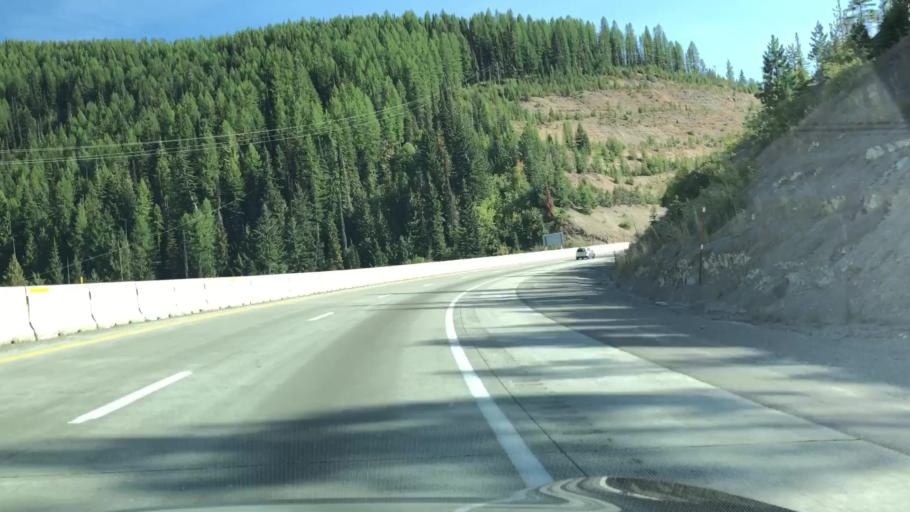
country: US
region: Idaho
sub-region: Shoshone County
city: Wallace
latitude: 47.4615
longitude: -115.6945
